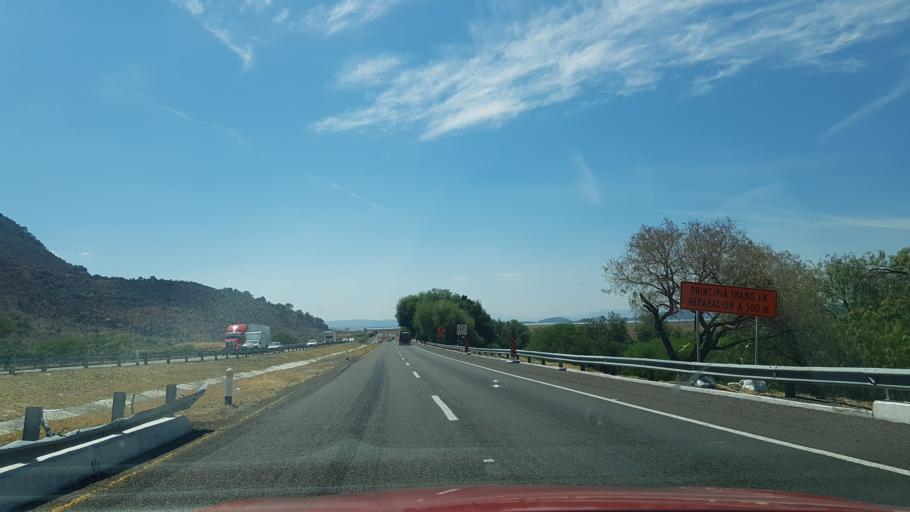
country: MX
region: Michoacan
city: Zinapecuaro
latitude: 19.9012
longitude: -100.8499
